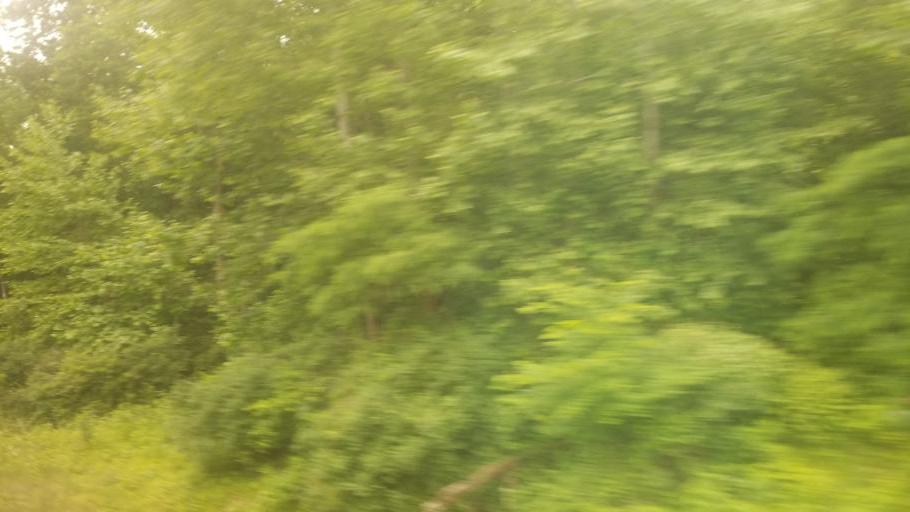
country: US
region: West Virginia
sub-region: Morgan County
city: Berkeley Springs
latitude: 39.6066
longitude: -78.3904
